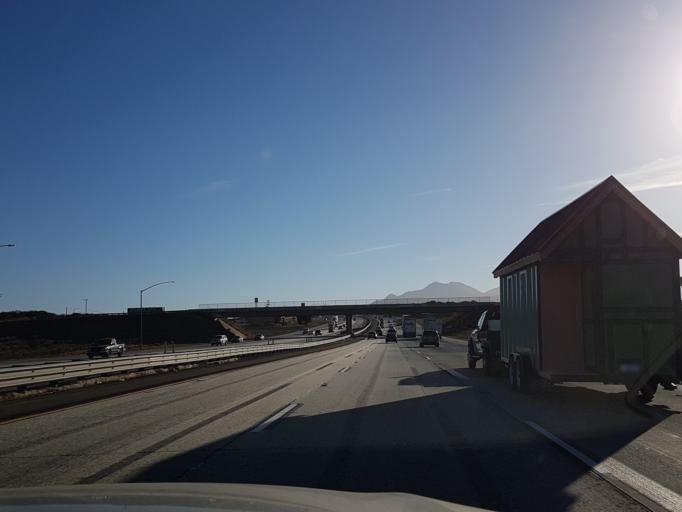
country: US
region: California
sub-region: San Bernardino County
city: Oak Hills
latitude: 34.3640
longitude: -117.4319
